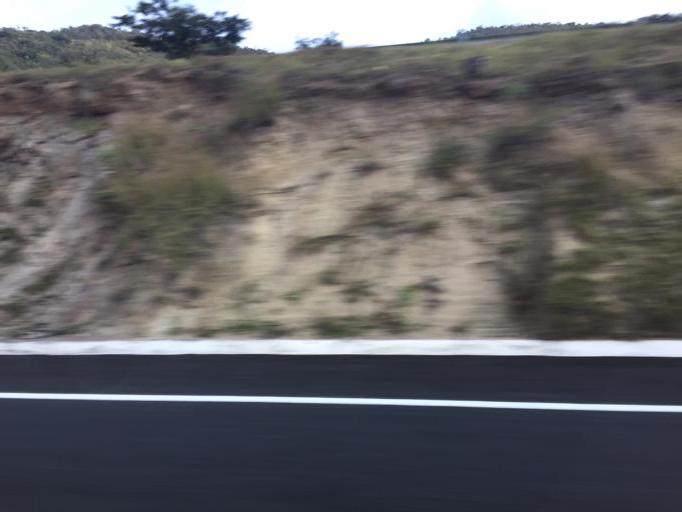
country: MX
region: Michoacan
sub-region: Cuitzeo
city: San Juan Benito Juarez (San Juan Tararameo)
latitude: 19.8961
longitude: -101.1481
